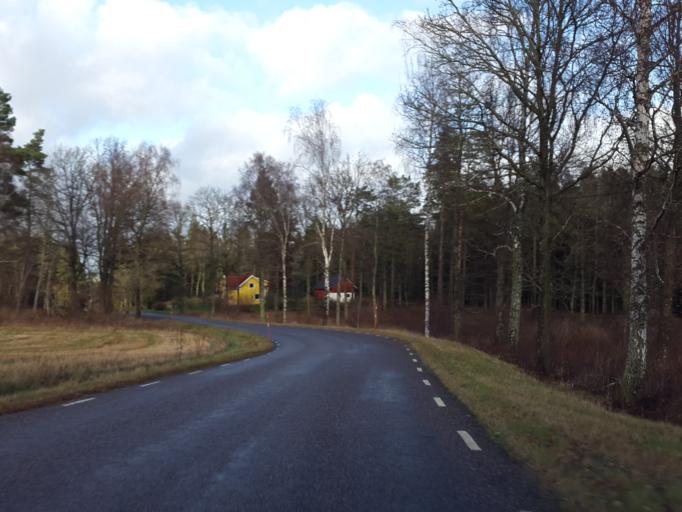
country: SE
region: Vaestra Goetaland
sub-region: Vargarda Kommun
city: Jonstorp
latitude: 58.0007
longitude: 12.7600
